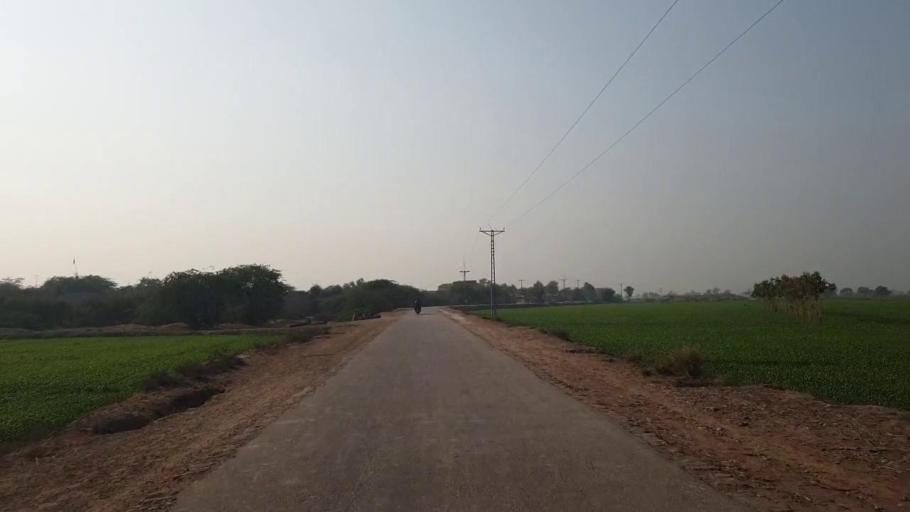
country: PK
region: Sindh
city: Shahdadpur
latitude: 25.9644
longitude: 68.5813
